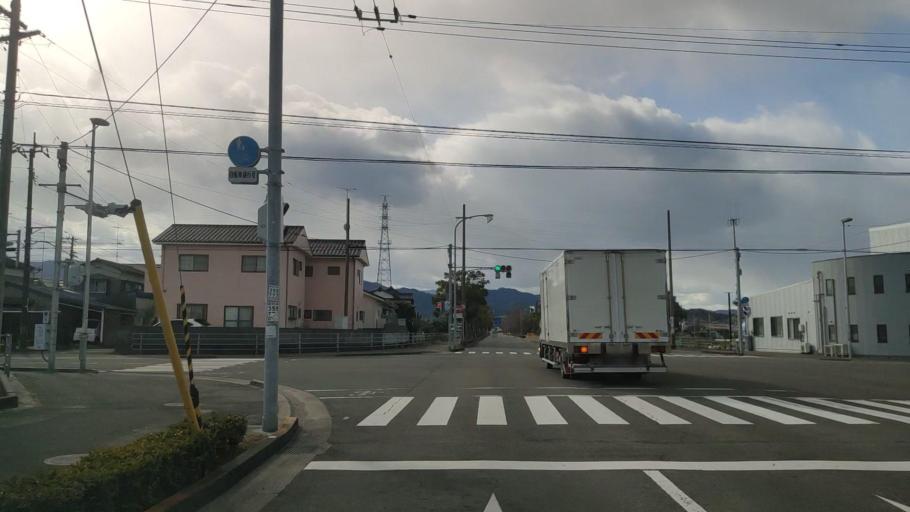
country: JP
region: Ehime
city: Saijo
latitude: 34.0414
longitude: 133.0014
